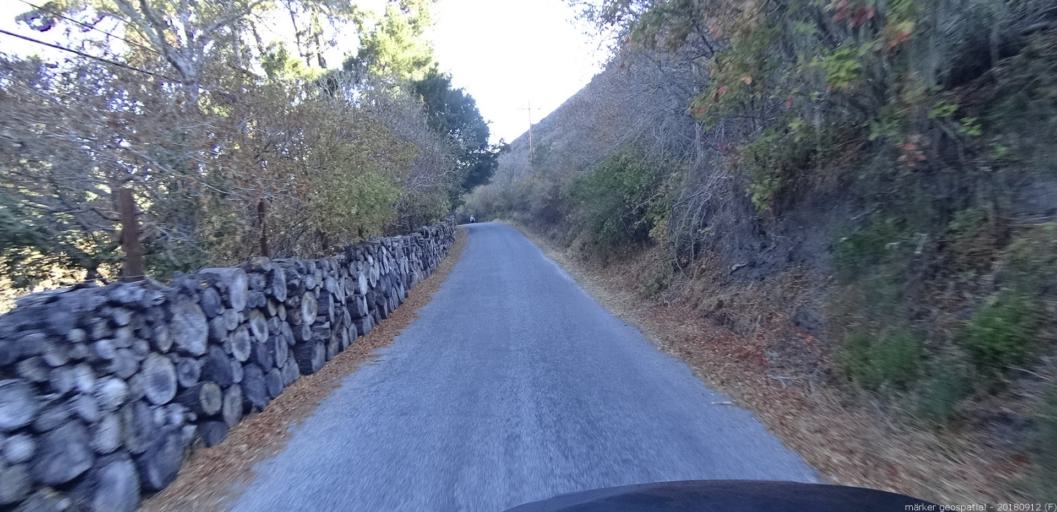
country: US
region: California
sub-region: Monterey County
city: Carmel Valley Village
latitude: 36.5355
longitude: -121.7382
